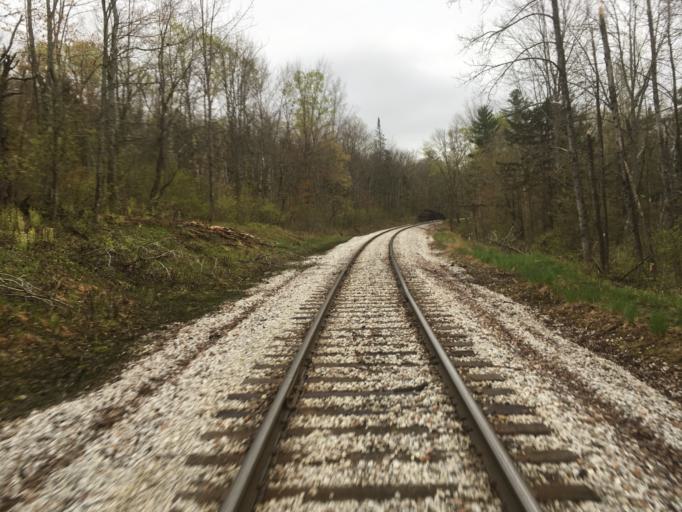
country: US
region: Vermont
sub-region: Rutland County
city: Rutland
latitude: 43.4735
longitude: -72.8714
